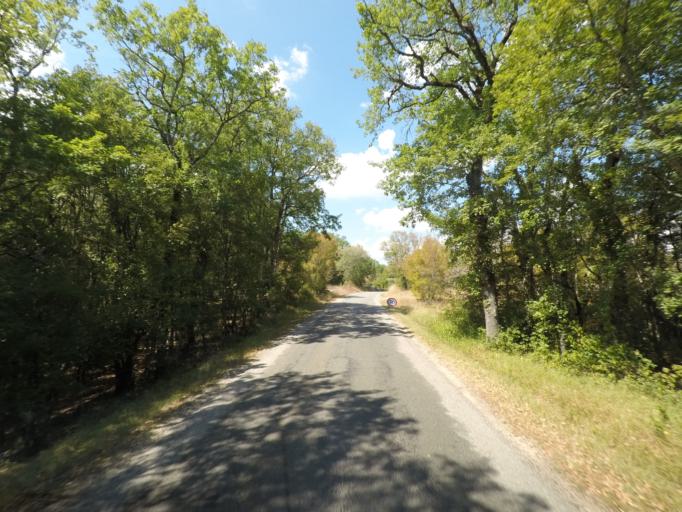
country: FR
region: Midi-Pyrenees
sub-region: Departement du Lot
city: Cahors
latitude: 44.5453
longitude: 1.5954
